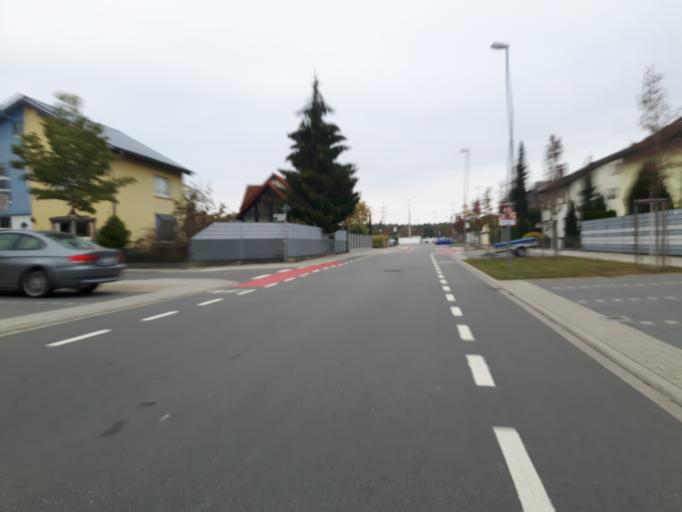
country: DE
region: Baden-Wuerttemberg
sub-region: Karlsruhe Region
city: Reilingen
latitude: 49.2885
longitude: 8.5599
